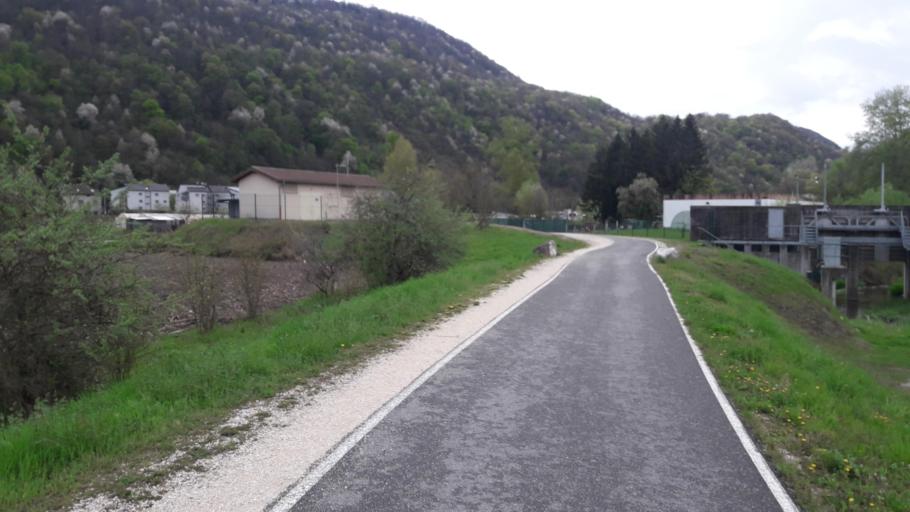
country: FR
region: Rhone-Alpes
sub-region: Departement de l'Isere
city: Gieres
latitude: 45.1905
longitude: 5.8078
